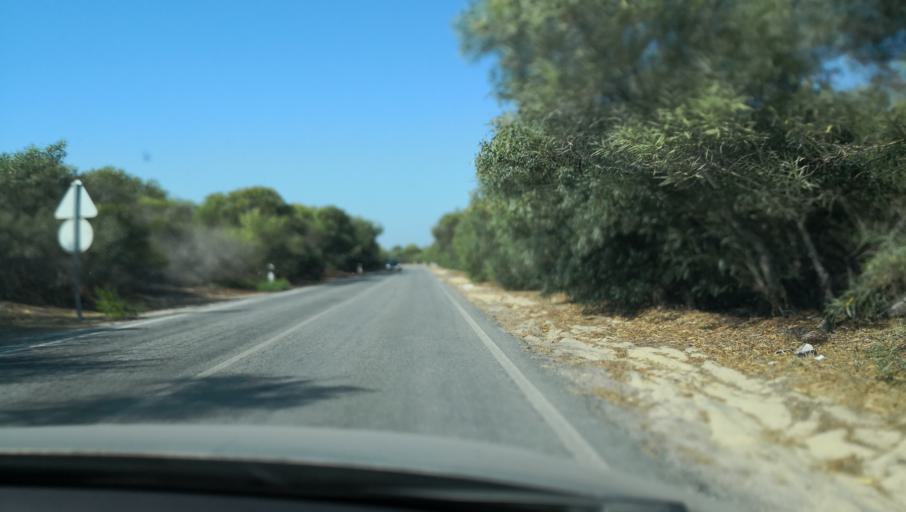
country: PT
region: Setubal
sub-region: Setubal
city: Setubal
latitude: 38.3875
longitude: -8.8000
